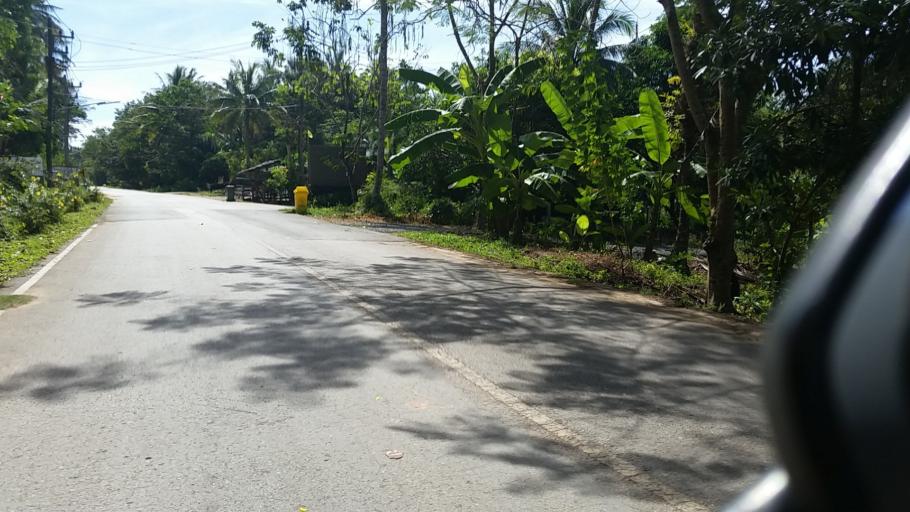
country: TH
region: Trat
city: Ko Chang Tai
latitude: 11.9889
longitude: 102.3976
